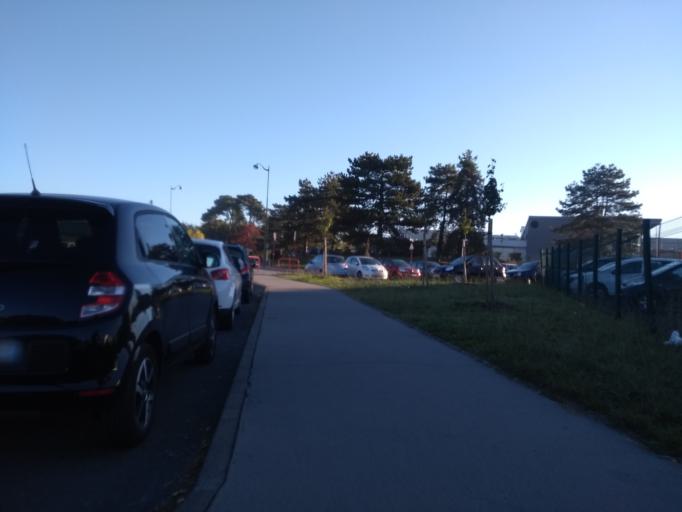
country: FR
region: Aquitaine
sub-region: Departement de la Gironde
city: Pessac
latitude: 44.7971
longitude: -0.6207
